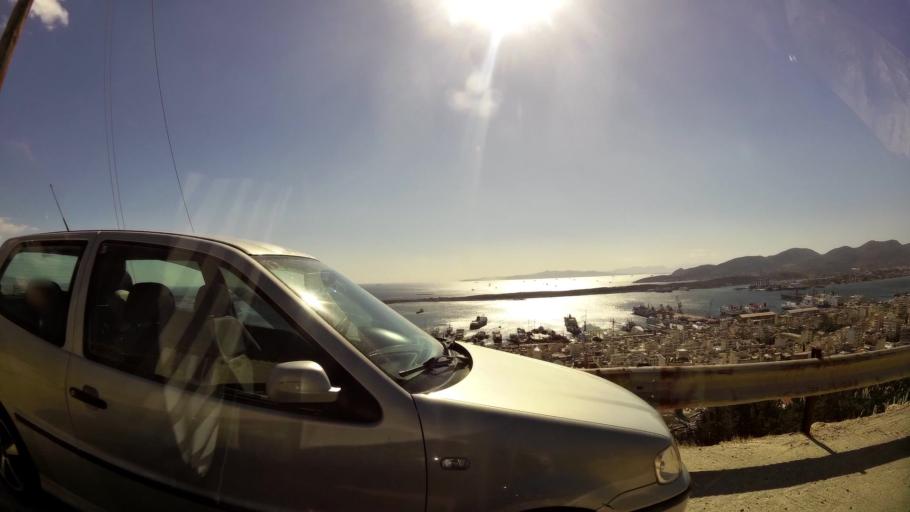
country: GR
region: Attica
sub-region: Nomos Piraios
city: Perama
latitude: 37.9701
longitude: 23.5701
